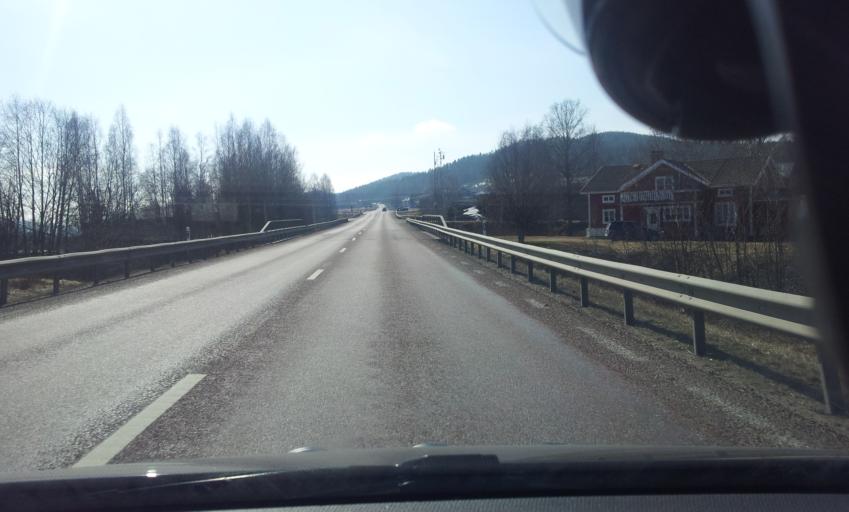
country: SE
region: Gaevleborg
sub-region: Ljusdals Kommun
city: Jaervsoe
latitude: 61.7542
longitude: 16.1610
